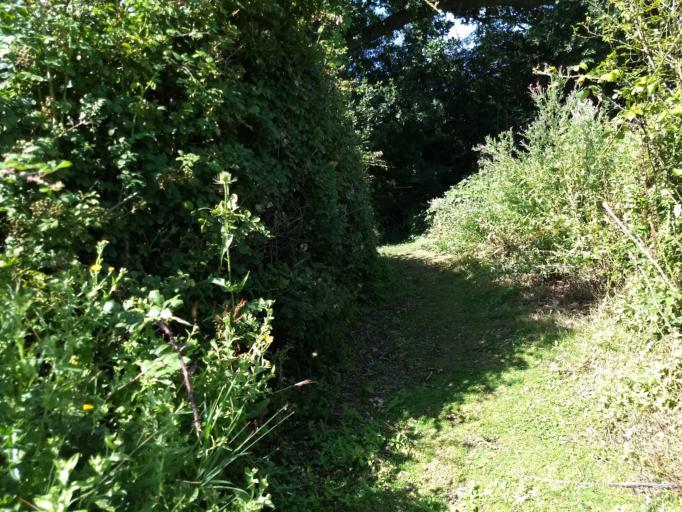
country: GB
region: England
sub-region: Isle of Wight
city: Ryde
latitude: 50.7108
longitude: -1.1624
